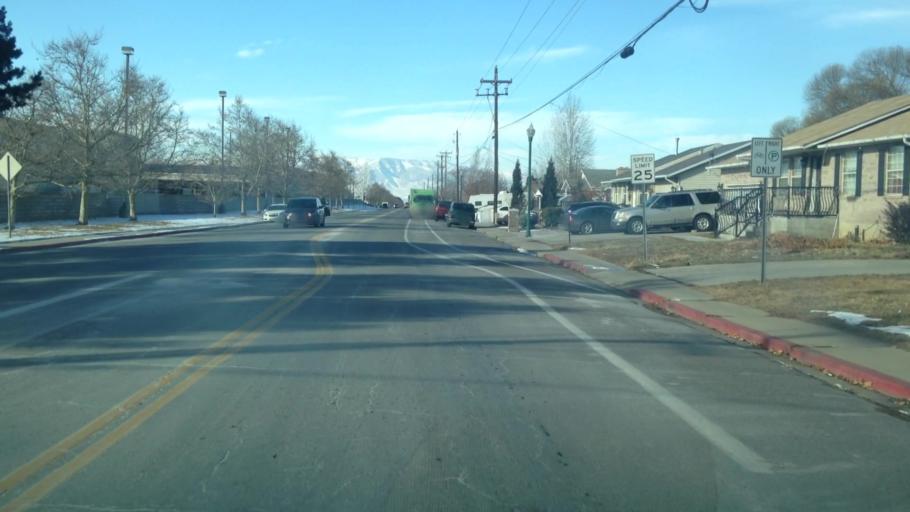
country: US
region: Utah
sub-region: Utah County
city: Orem
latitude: 40.2753
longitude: -111.6954
